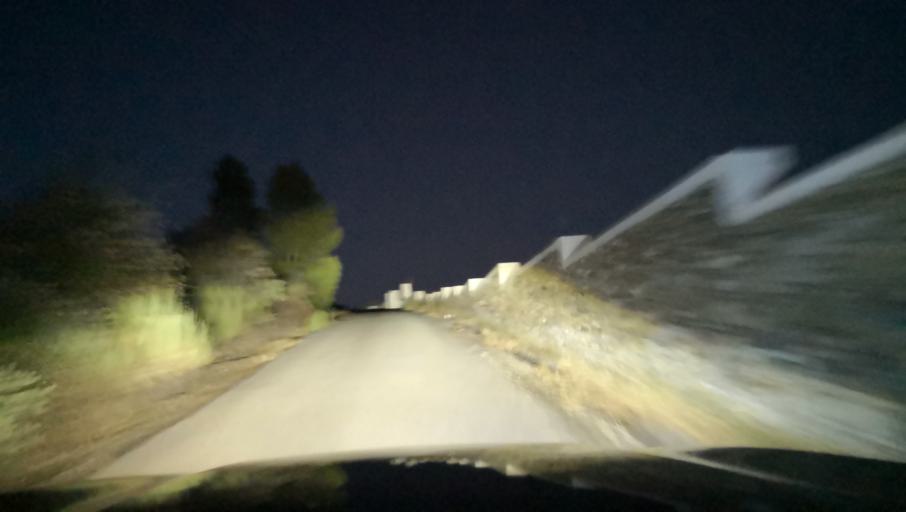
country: PT
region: Viseu
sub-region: Armamar
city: Armamar
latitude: 41.1516
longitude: -7.6960
